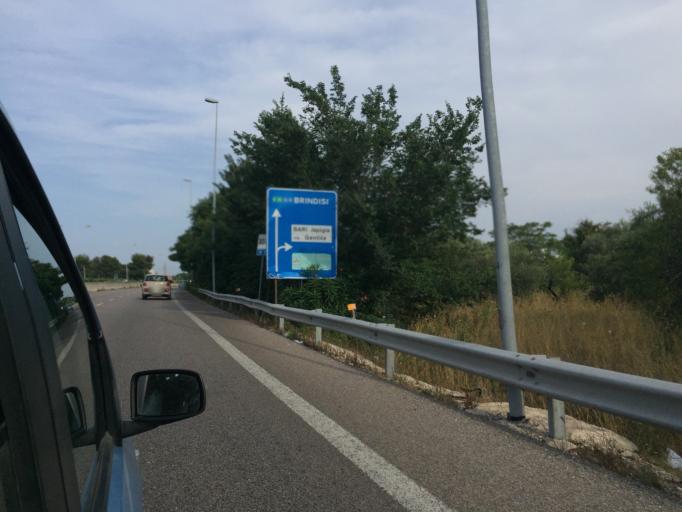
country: IT
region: Apulia
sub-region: Provincia di Bari
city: Triggiano
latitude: 41.1013
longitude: 16.9280
